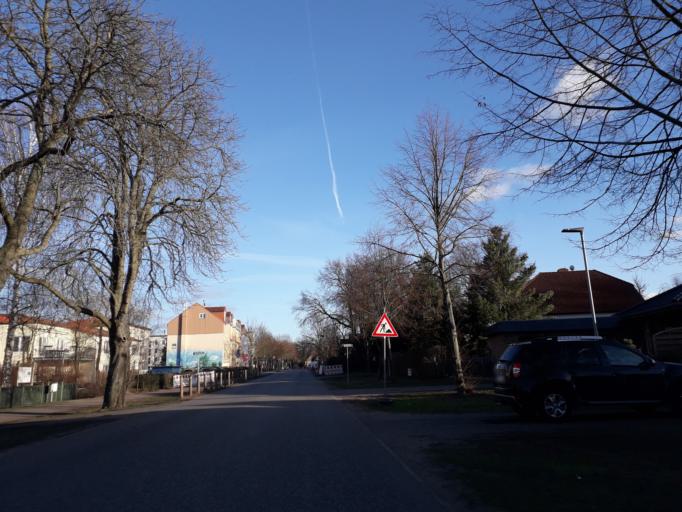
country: DE
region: Brandenburg
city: Brieselang
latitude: 52.5846
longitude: 12.9852
